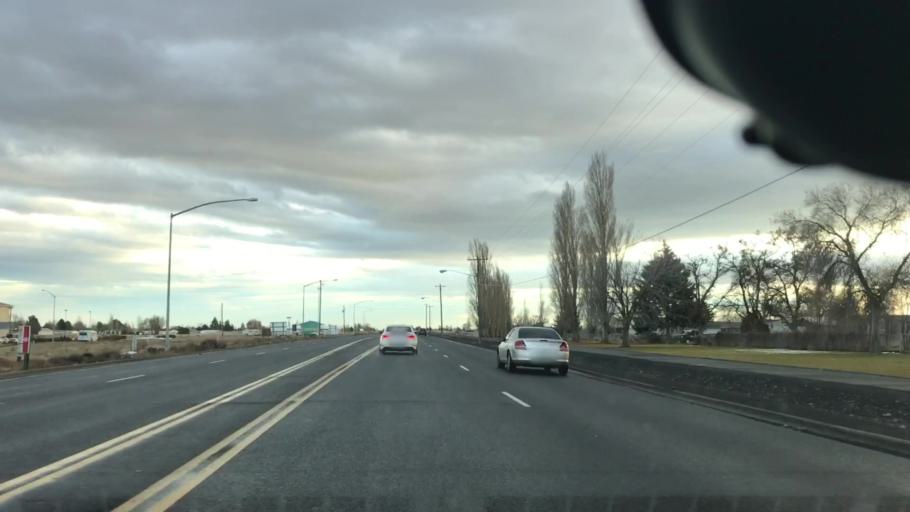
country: US
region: Washington
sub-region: Grant County
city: Moses Lake North
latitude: 47.1631
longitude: -119.3136
